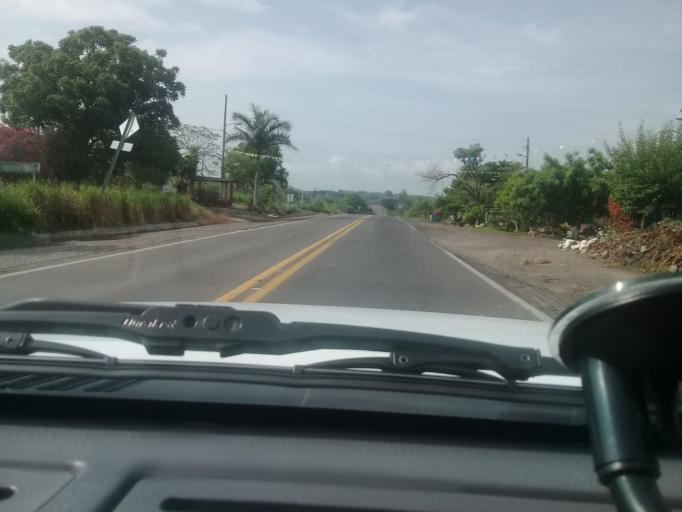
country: MX
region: Veracruz
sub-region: Paso de Ovejas
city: Tolome
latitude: 19.2639
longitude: -96.3736
